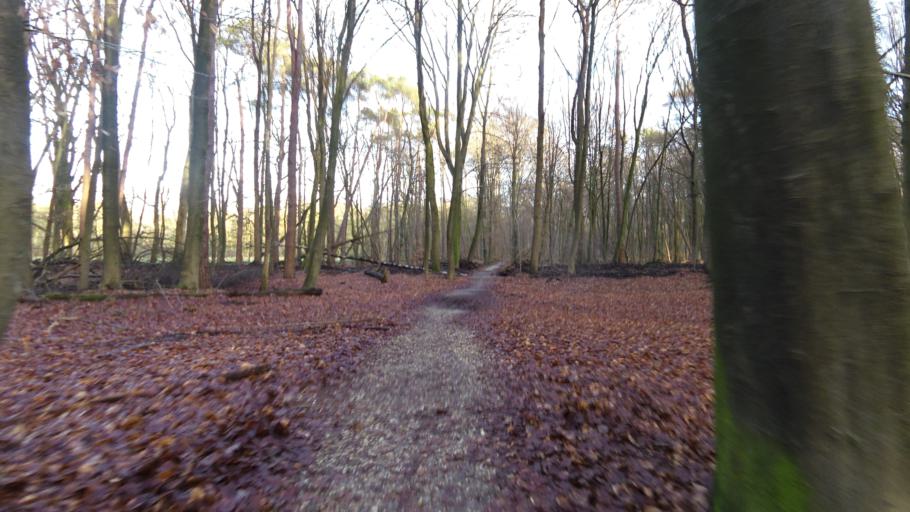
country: NL
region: Gelderland
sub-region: Gemeente Epe
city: Vaassen
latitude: 52.2861
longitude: 5.9132
